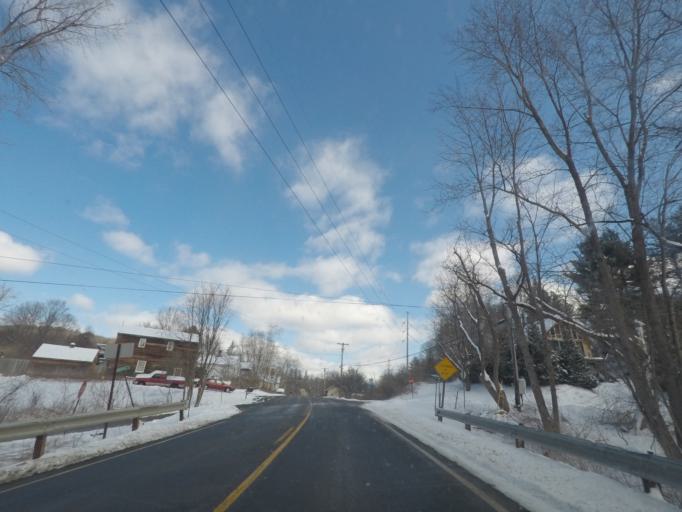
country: US
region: New York
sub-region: Rensselaer County
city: Nassau
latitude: 42.4926
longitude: -73.5143
